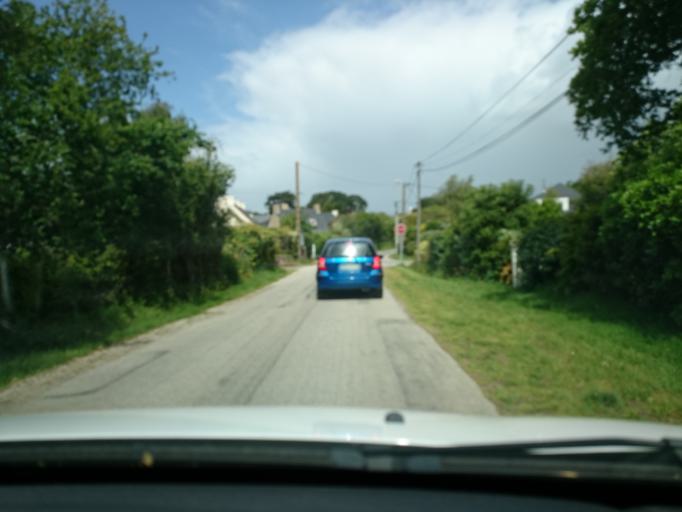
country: FR
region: Brittany
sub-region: Departement du Morbihan
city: Larmor-Baden
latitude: 47.5860
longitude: -2.9026
